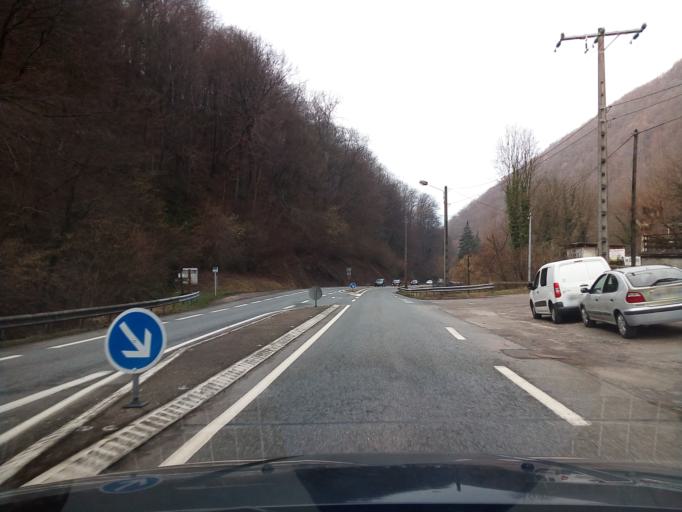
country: FR
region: Rhone-Alpes
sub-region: Departement de l'Isere
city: Gieres
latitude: 45.1631
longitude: 5.8129
